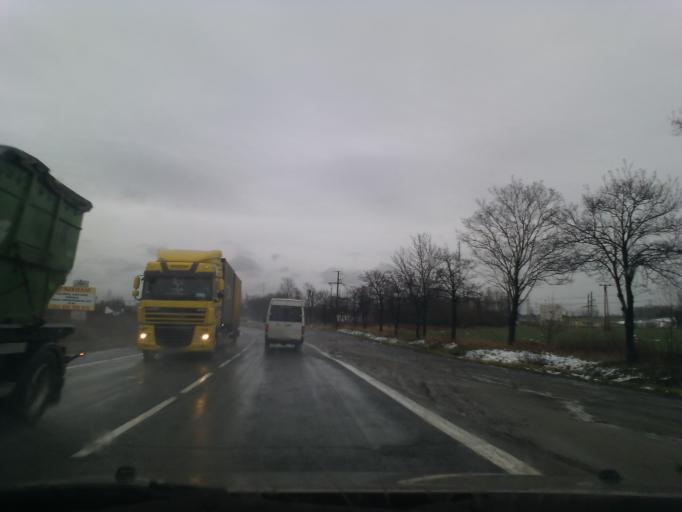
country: PL
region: Lower Silesian Voivodeship
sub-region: Powiat swidnicki
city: Swiebodzice
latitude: 50.8550
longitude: 16.3463
